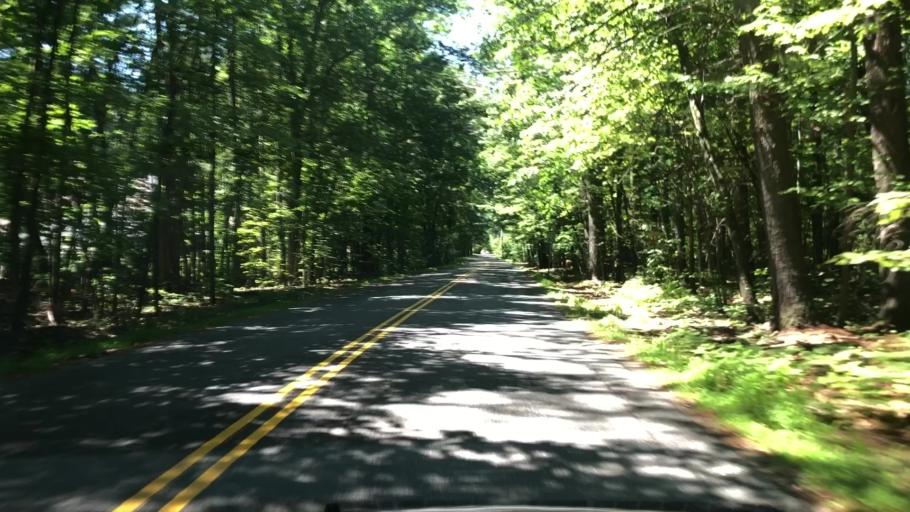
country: US
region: New Hampshire
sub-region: Hillsborough County
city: Milford
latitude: 42.8393
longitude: -71.5709
